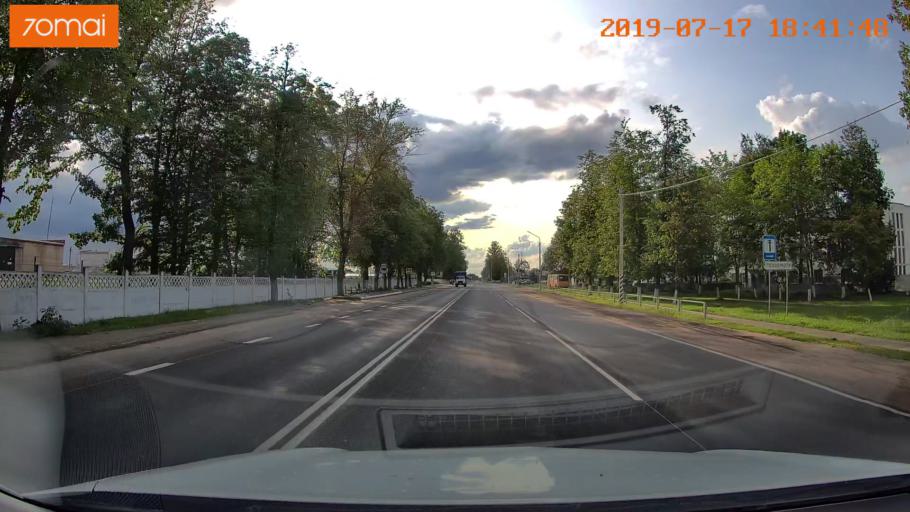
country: BY
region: Mogilev
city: Asipovichy
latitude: 53.3073
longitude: 28.6576
